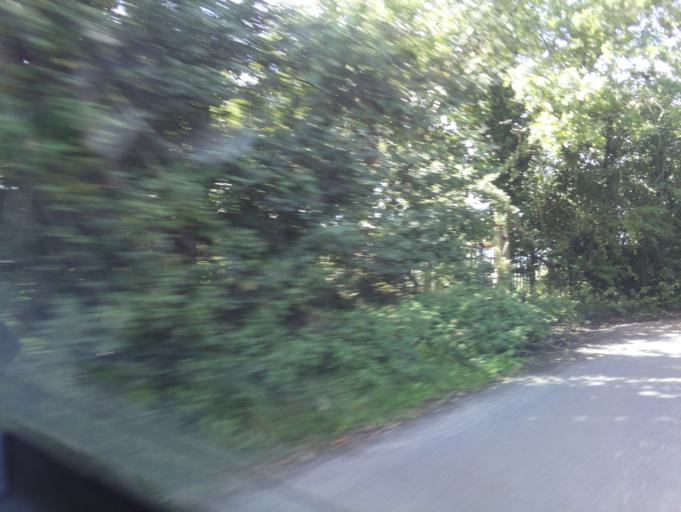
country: GB
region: England
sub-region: Wiltshire
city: Erlestoke
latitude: 51.2826
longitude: -2.0669
